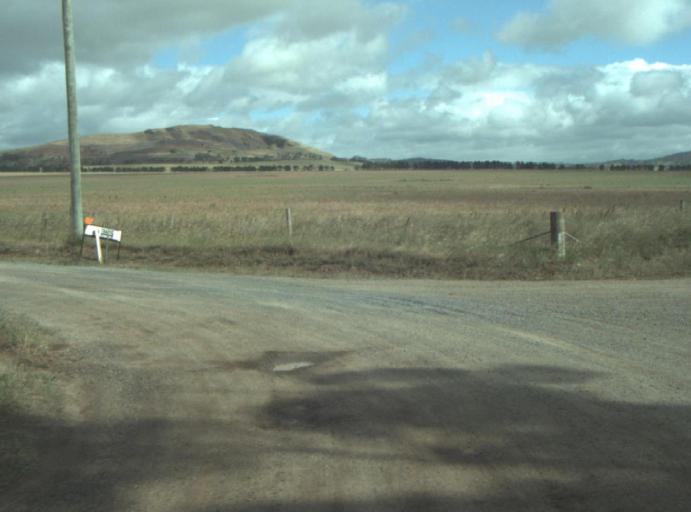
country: AU
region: Victoria
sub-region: Greater Geelong
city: Lara
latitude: -37.9225
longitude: 144.3133
